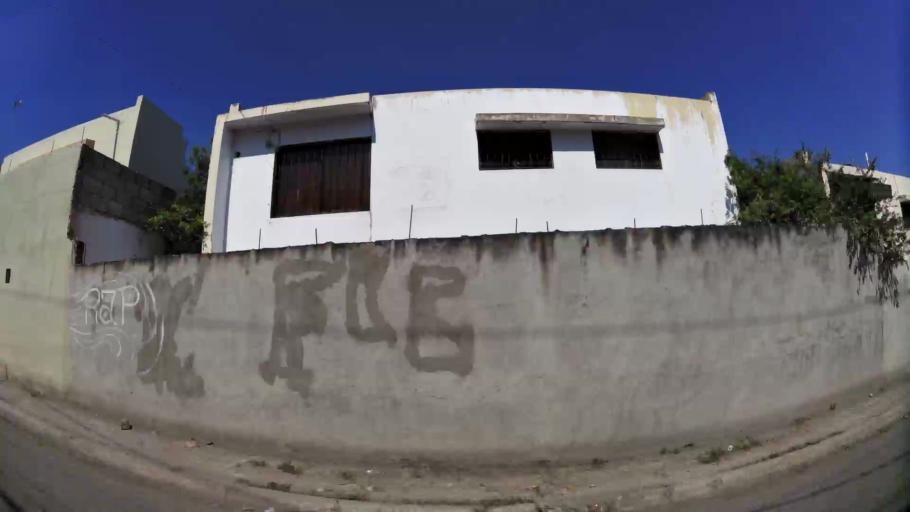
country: DO
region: Santo Domingo
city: Santo Domingo Oeste
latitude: 18.4761
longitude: -70.0006
